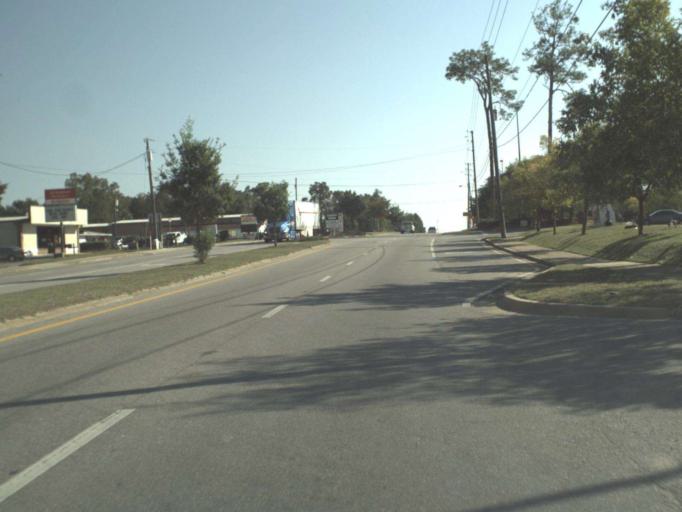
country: US
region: Florida
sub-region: Walton County
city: DeFuniak Springs
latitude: 30.7052
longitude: -86.1227
